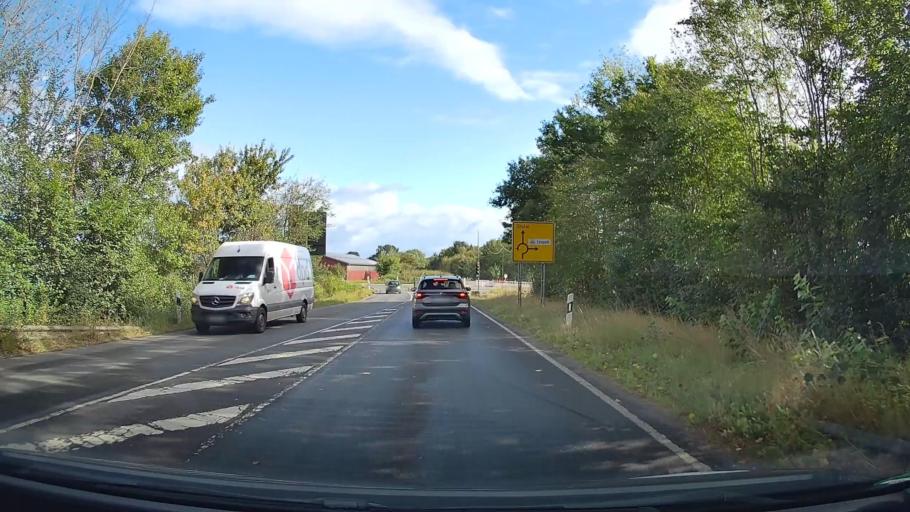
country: DE
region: Lower Saxony
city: Driftsethe
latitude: 53.4431
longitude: 8.5865
